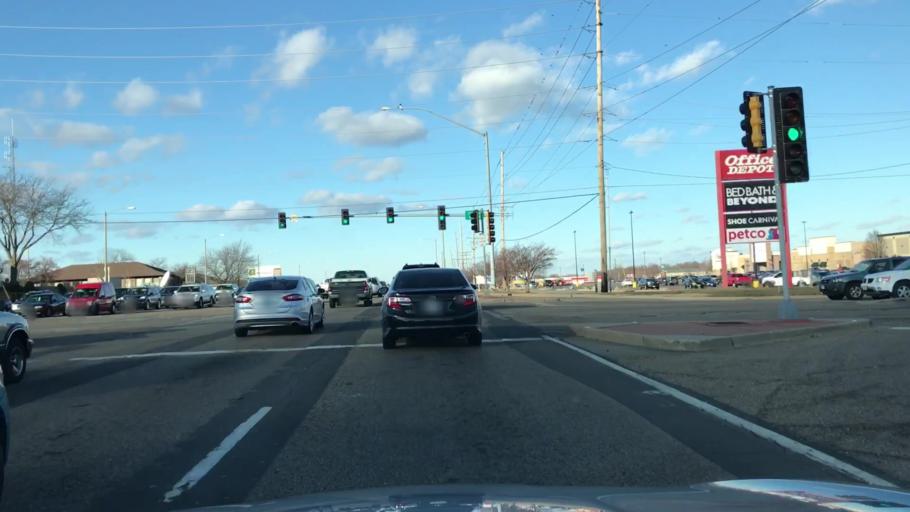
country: US
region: Illinois
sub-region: McLean County
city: Normal
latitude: 40.5102
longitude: -88.9532
